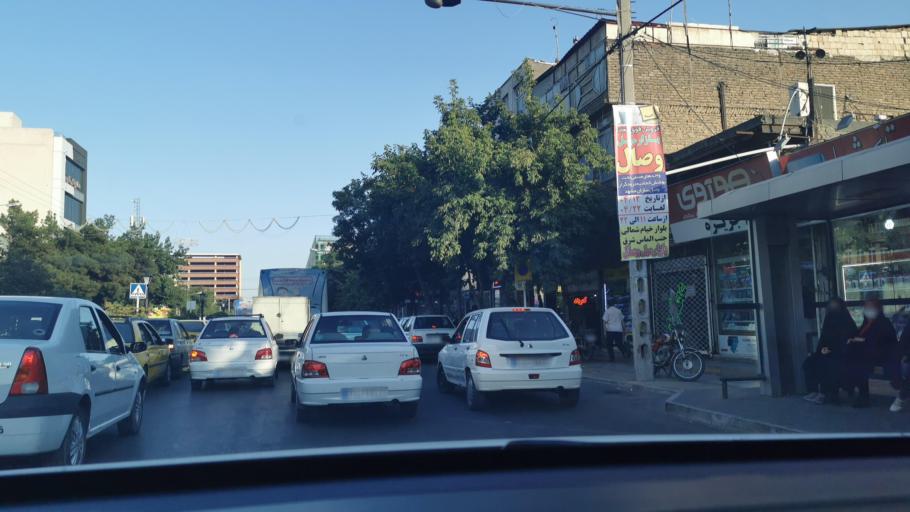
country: IR
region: Razavi Khorasan
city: Mashhad
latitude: 36.2943
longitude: 59.6450
